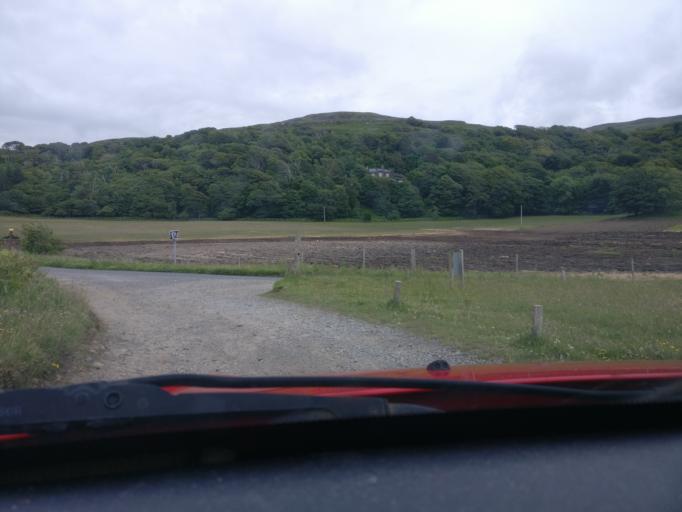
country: GB
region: Scotland
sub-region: Argyll and Bute
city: Isle Of Mull
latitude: 56.5803
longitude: -6.2773
